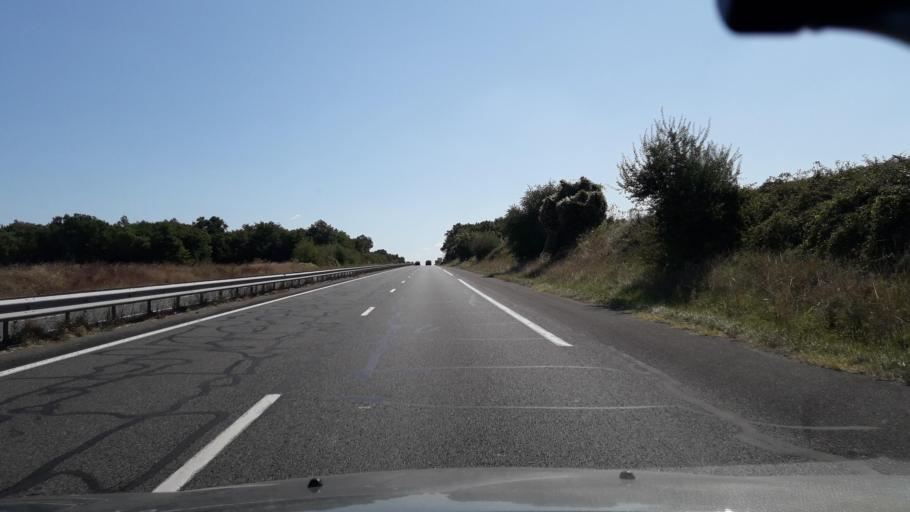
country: FR
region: Poitou-Charentes
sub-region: Departement de la Charente
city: Saint-Meme-les-Carrieres
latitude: 45.6957
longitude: -0.1096
